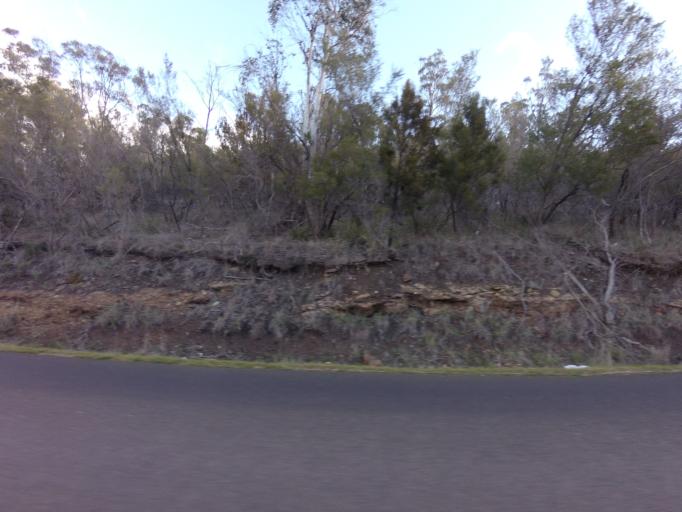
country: AU
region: Tasmania
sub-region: Derwent Valley
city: New Norfolk
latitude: -42.7362
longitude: 147.0338
